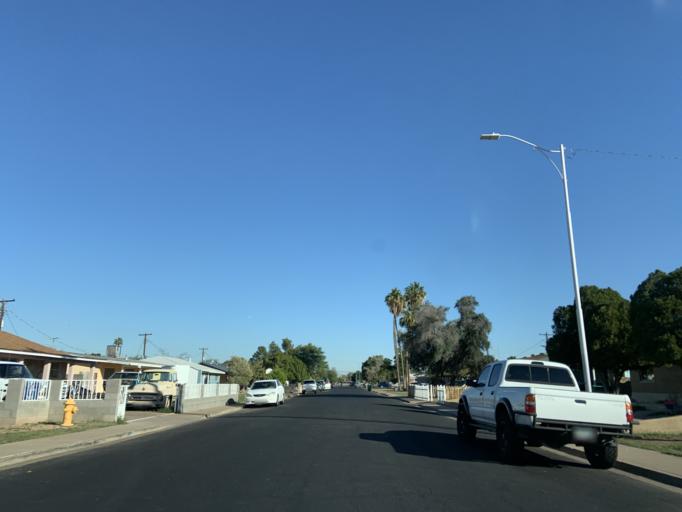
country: US
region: Arizona
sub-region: Maricopa County
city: Mesa
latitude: 33.4021
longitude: -111.8639
